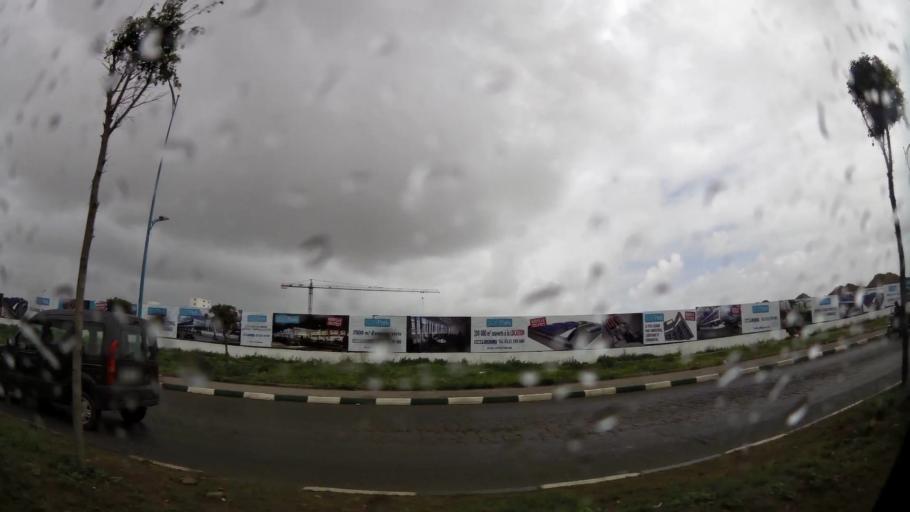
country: MA
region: Grand Casablanca
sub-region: Mediouna
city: Tit Mellil
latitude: 33.6222
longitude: -7.5021
